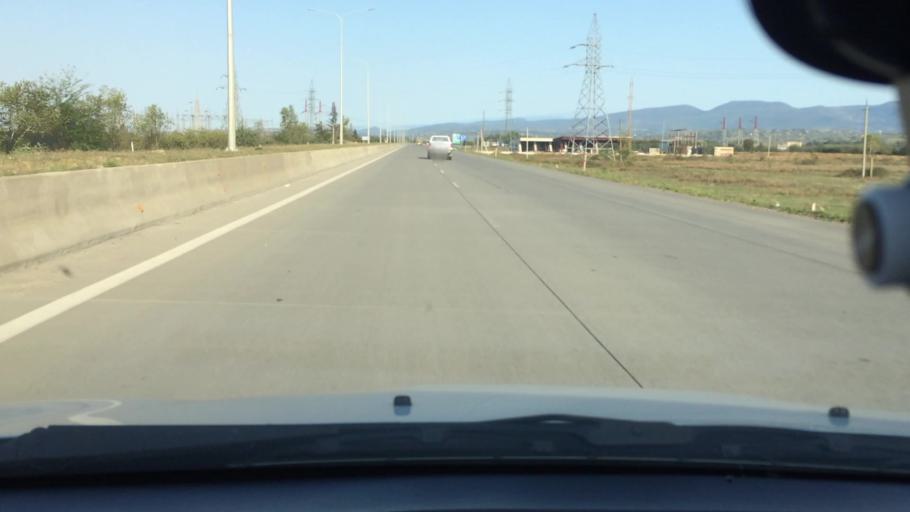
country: GE
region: Imereti
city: Zestap'oni
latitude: 42.1442
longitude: 42.9688
